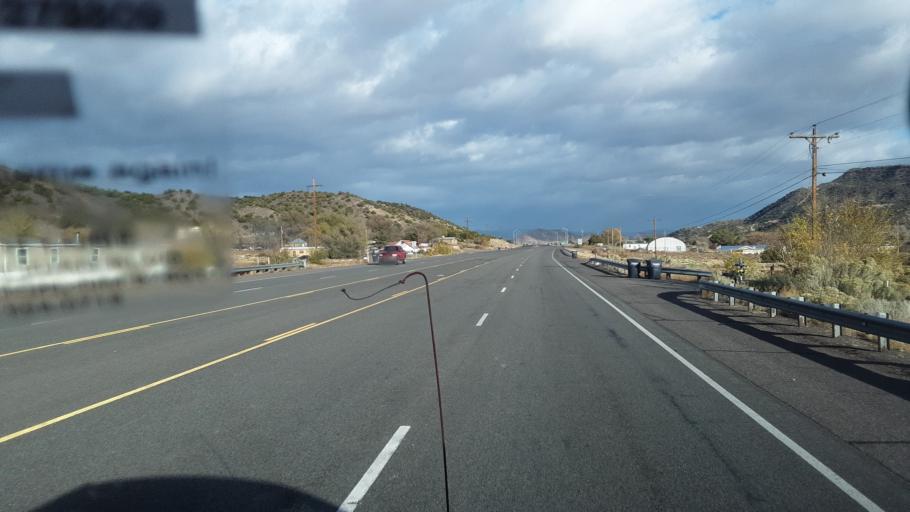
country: US
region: New Mexico
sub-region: Rio Arriba County
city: Ohkay Owingeh
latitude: 36.0672
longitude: -106.1222
